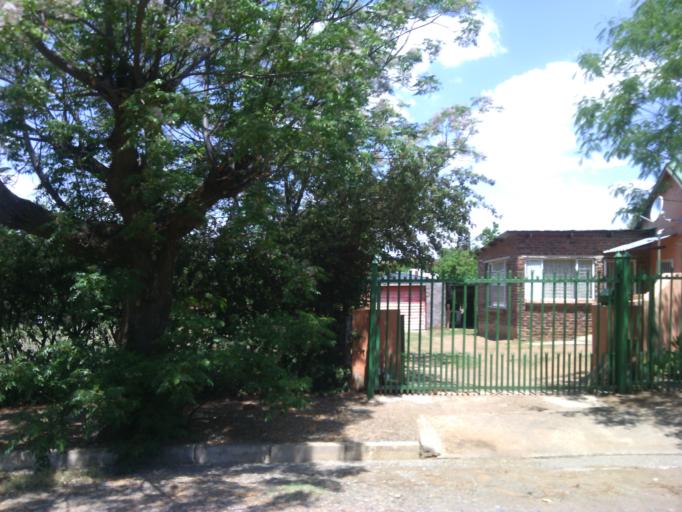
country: ZA
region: Orange Free State
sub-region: Xhariep District Municipality
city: Dewetsdorp
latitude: -29.5785
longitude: 26.6661
